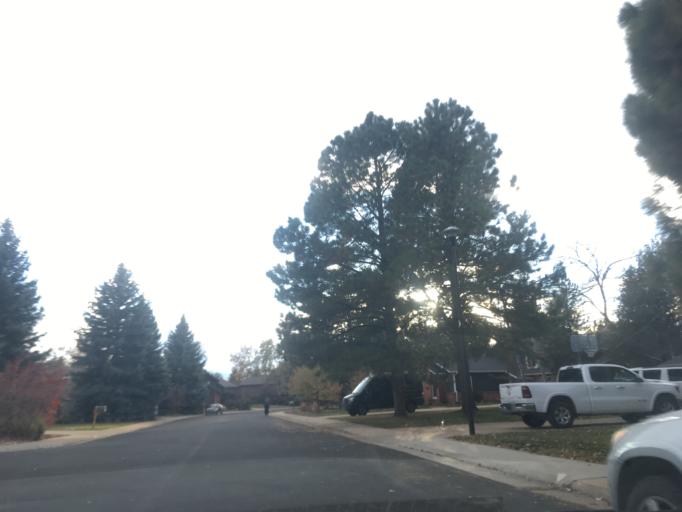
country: US
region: Colorado
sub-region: Boulder County
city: Louisville
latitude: 39.9892
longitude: -105.1604
